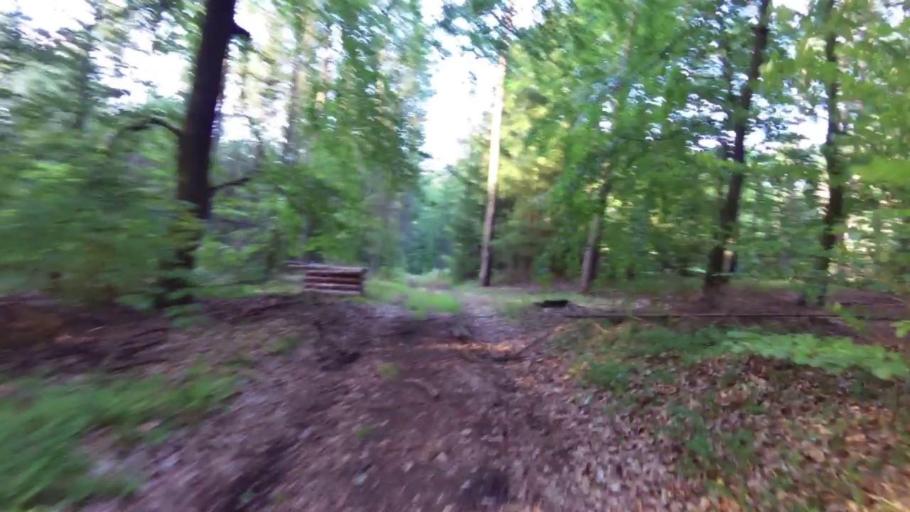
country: PL
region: West Pomeranian Voivodeship
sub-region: Powiat drawski
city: Zlocieniec
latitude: 53.5625
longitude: 16.0189
